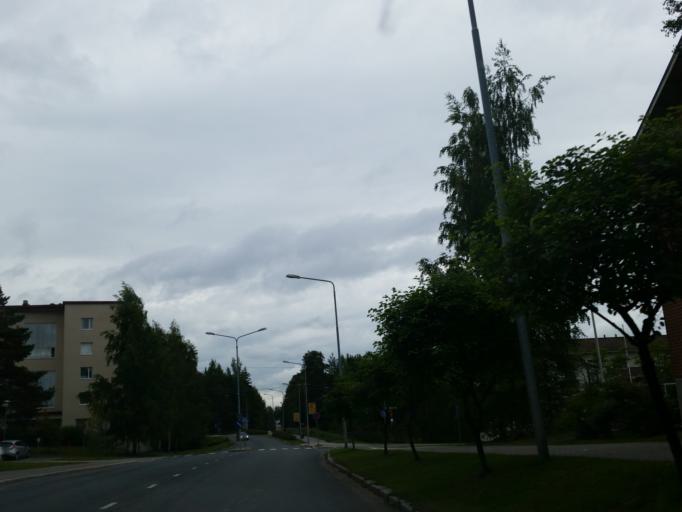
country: FI
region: Northern Savo
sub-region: Kuopio
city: Kuopio
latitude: 62.9028
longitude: 27.7059
